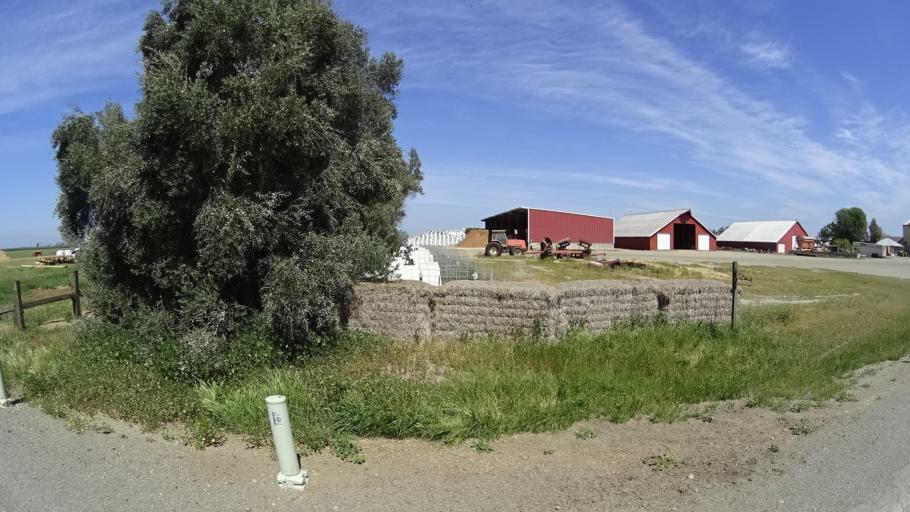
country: US
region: California
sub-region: Glenn County
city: Orland
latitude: 39.6531
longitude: -122.1699
